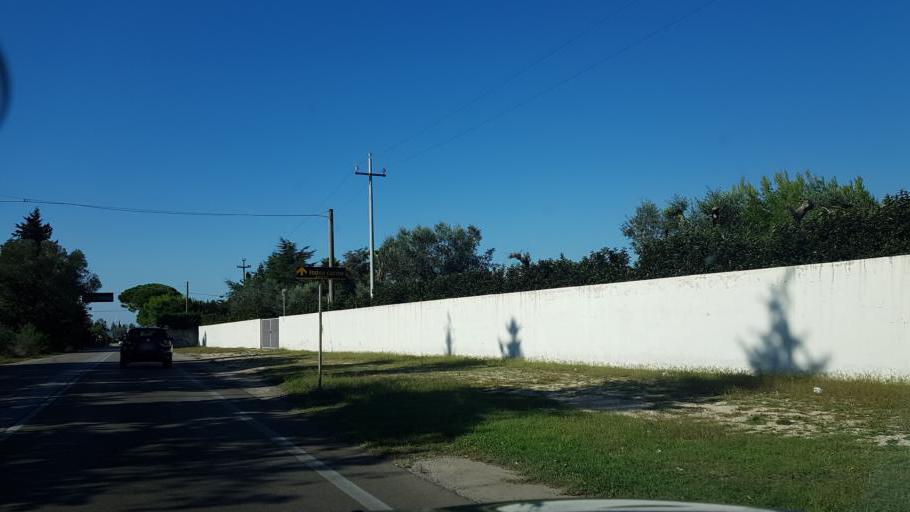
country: IT
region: Apulia
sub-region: Provincia di Lecce
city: Magliano
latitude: 40.3209
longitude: 18.0682
